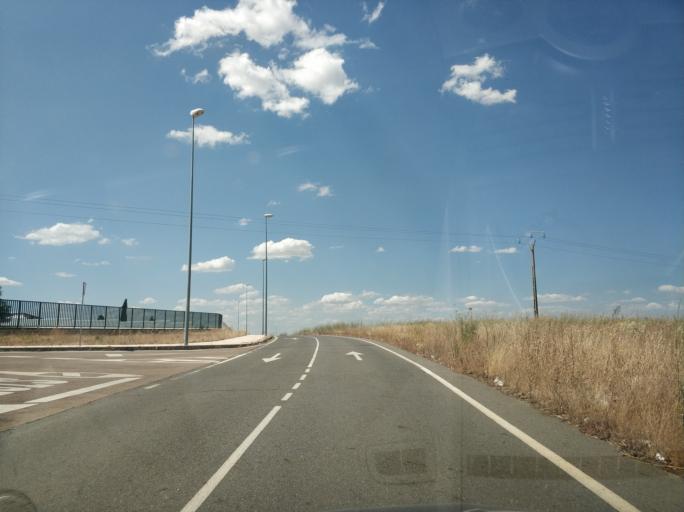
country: ES
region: Castille and Leon
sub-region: Provincia de Salamanca
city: Aldeatejada
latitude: 40.9472
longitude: -5.6935
